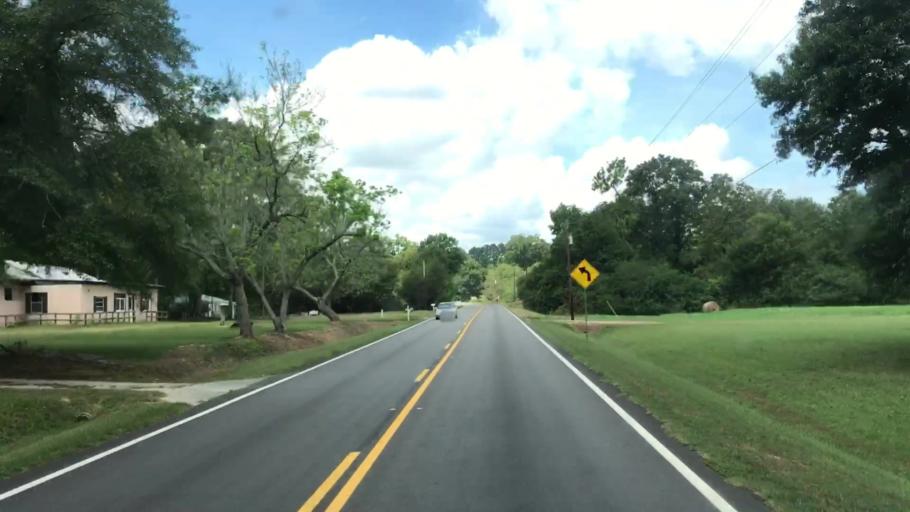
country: US
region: Georgia
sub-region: Greene County
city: Greensboro
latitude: 33.5641
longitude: -83.1451
